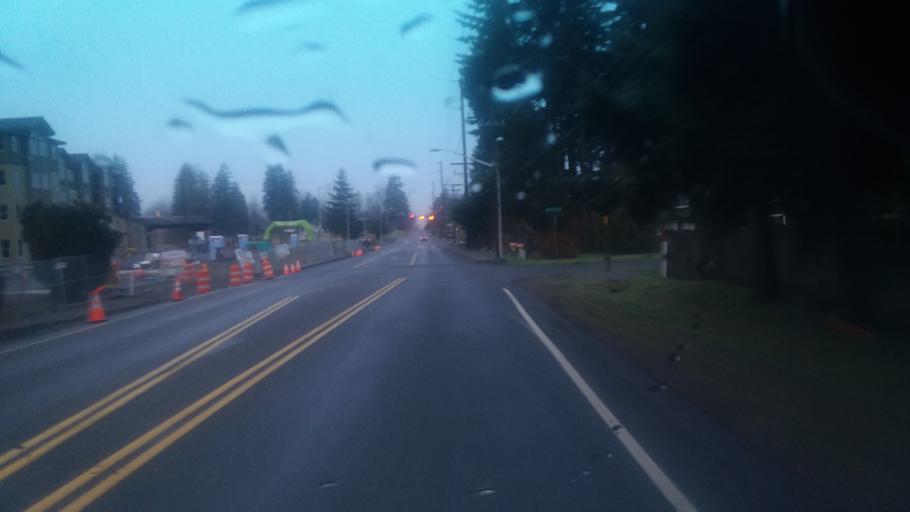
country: US
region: Washington
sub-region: Pierce County
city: South Hill
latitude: 47.1257
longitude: -122.2906
